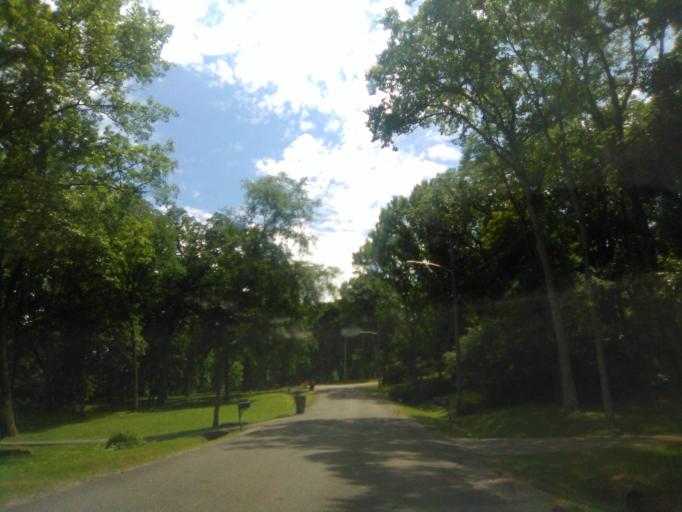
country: US
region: Tennessee
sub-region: Davidson County
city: Belle Meade
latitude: 36.1272
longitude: -86.8820
